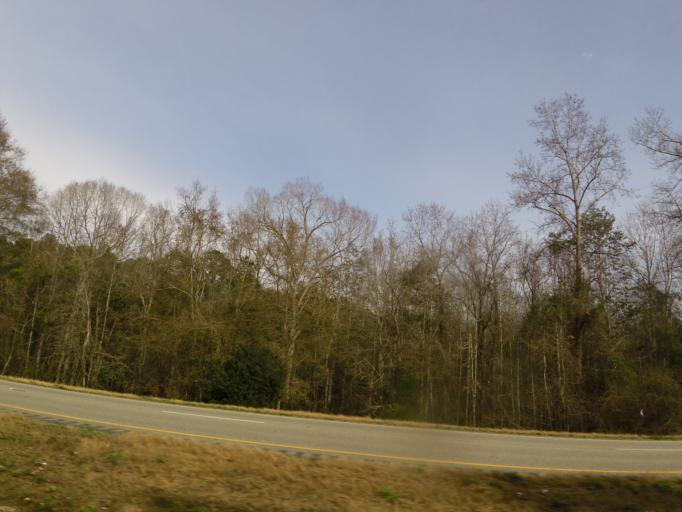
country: US
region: Alabama
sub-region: Dale County
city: Newton
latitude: 31.4018
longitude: -85.5934
